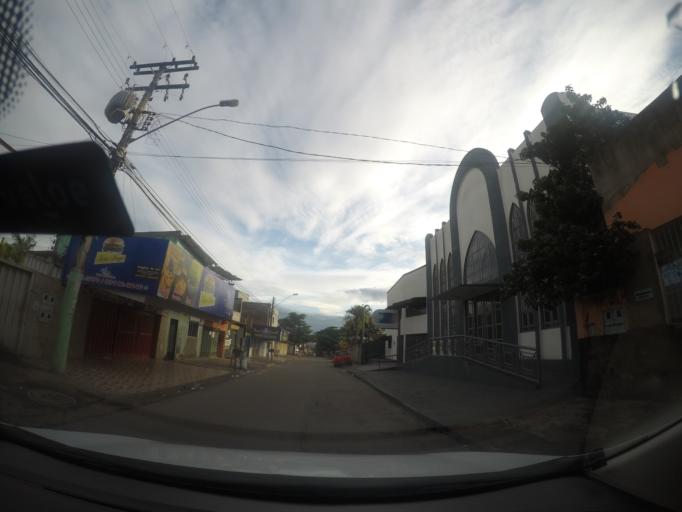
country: BR
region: Goias
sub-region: Goiania
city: Goiania
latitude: -16.6459
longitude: -49.3230
